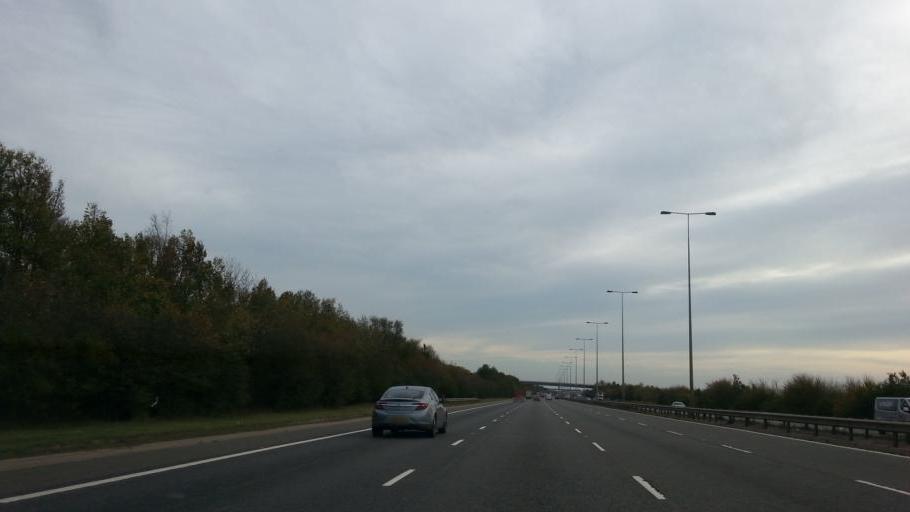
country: GB
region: England
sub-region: Cambridgeshire
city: Stilton
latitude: 52.4727
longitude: -0.2848
